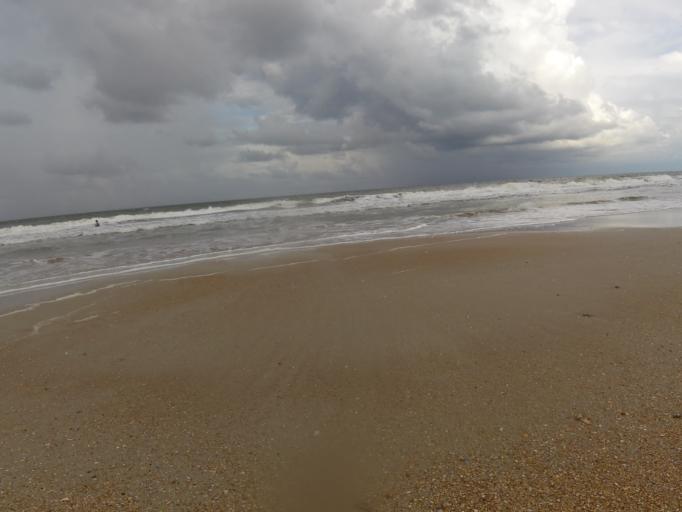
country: US
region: Florida
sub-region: Saint Johns County
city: Palm Valley
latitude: 30.0852
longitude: -81.3368
